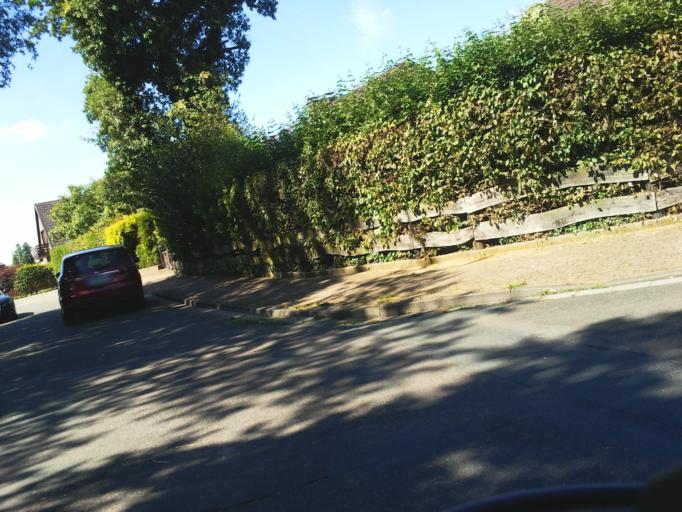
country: DE
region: Lower Saxony
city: Nienburg
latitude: 52.6656
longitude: 9.2307
